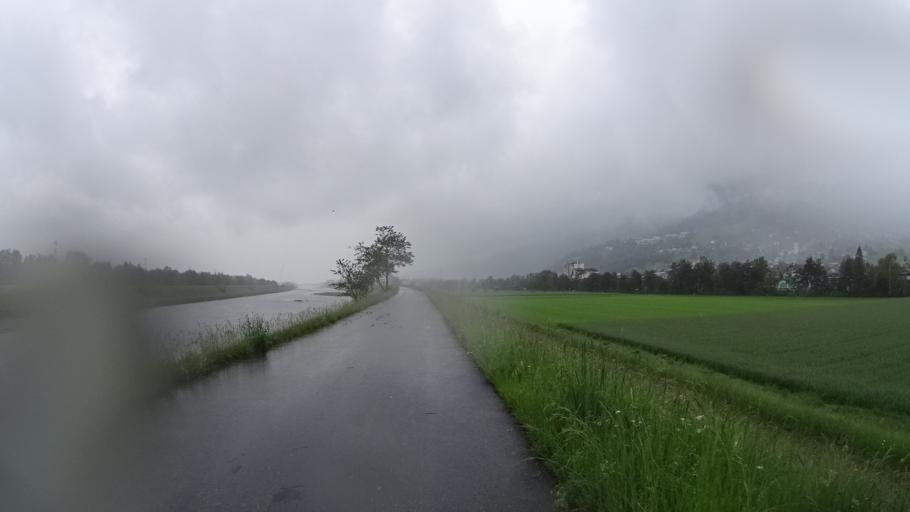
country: LI
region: Triesen
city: Triesen
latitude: 47.0986
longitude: 9.5206
